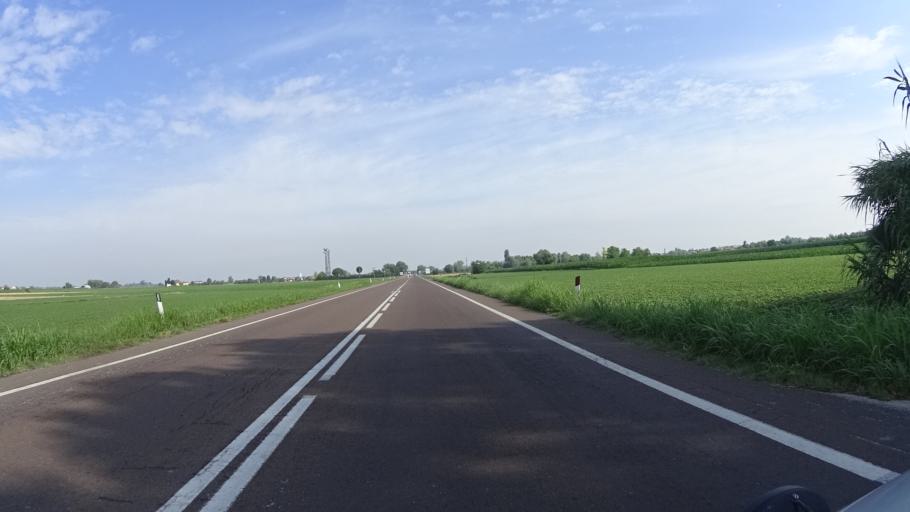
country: IT
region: Veneto
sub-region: Provincia di Venezia
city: San Michele al Tagliamento
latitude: 45.7512
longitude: 12.9893
